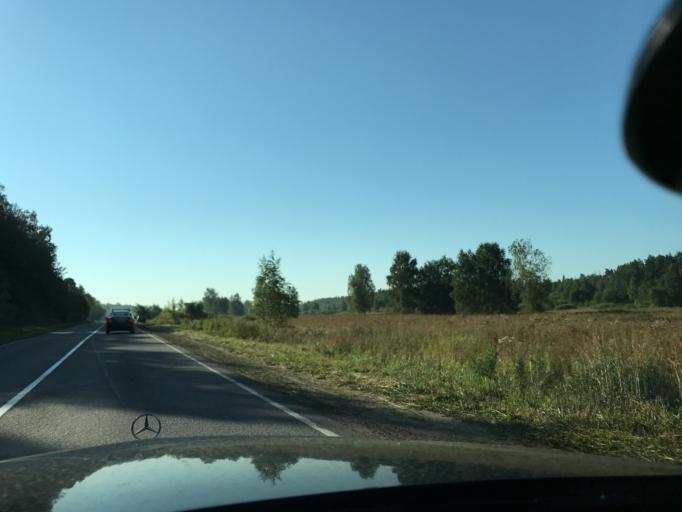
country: RU
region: Moskovskaya
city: Bakhchivandzhi
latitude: 55.8592
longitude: 38.0615
